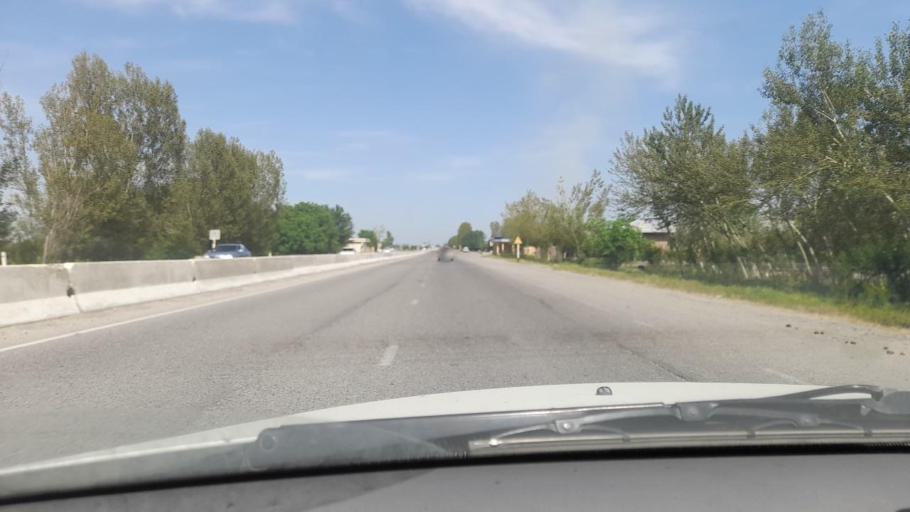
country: UZ
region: Samarqand
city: Kattaqo'rg'on
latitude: 39.9166
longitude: 66.3247
